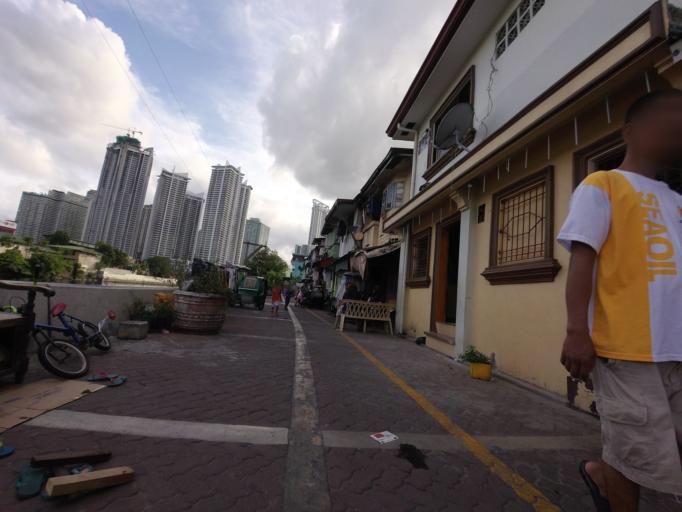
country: PH
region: Metro Manila
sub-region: Mandaluyong
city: Mandaluyong City
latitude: 14.5690
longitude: 121.0425
